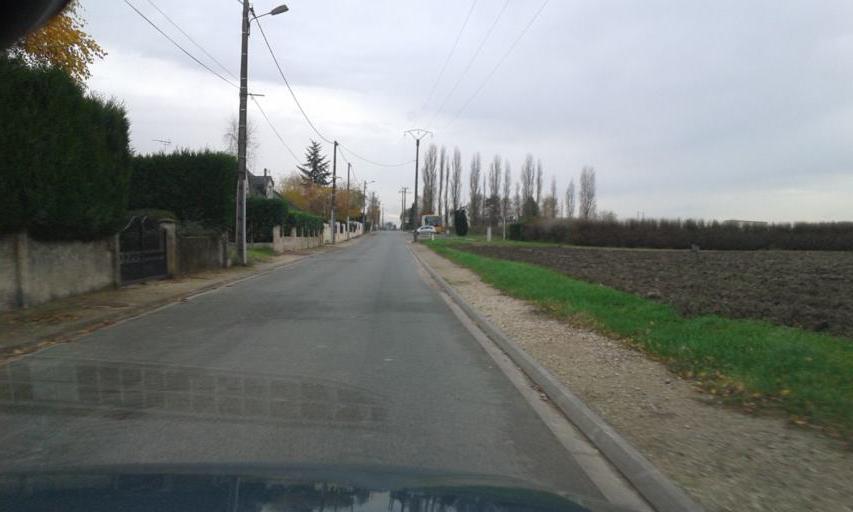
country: FR
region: Centre
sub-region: Departement du Loiret
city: Gidy
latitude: 47.9829
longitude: 1.8306
